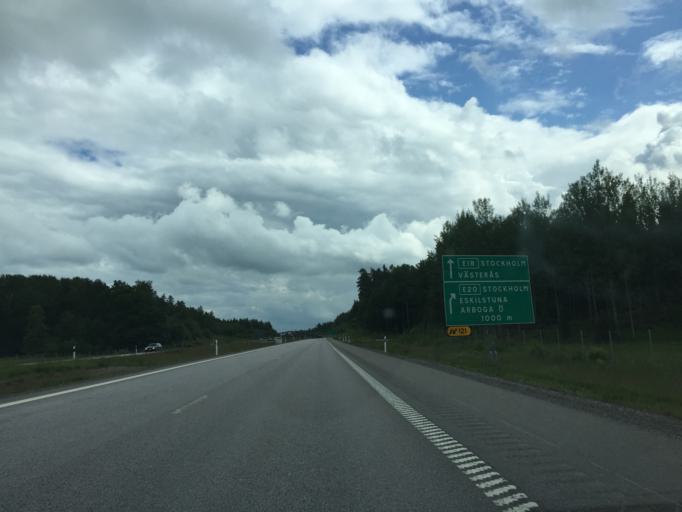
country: SE
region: Vaestmanland
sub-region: Arboga Kommun
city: Arboga
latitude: 59.4256
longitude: 15.8481
